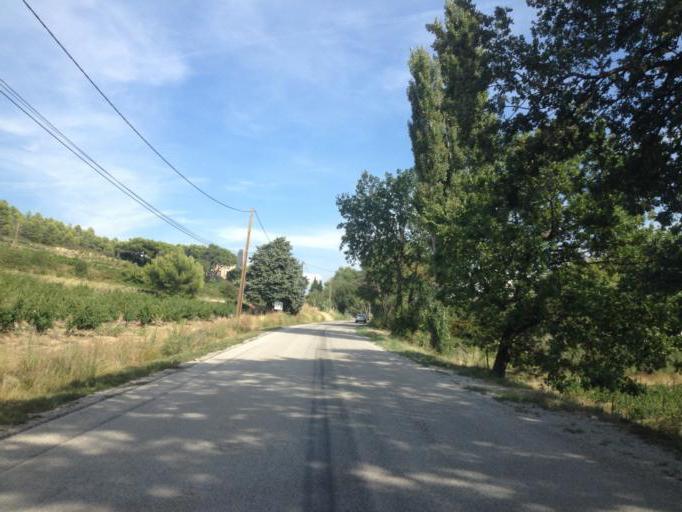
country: FR
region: Provence-Alpes-Cote d'Azur
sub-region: Departement du Vaucluse
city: Vacqueyras
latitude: 44.1378
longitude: 4.9997
